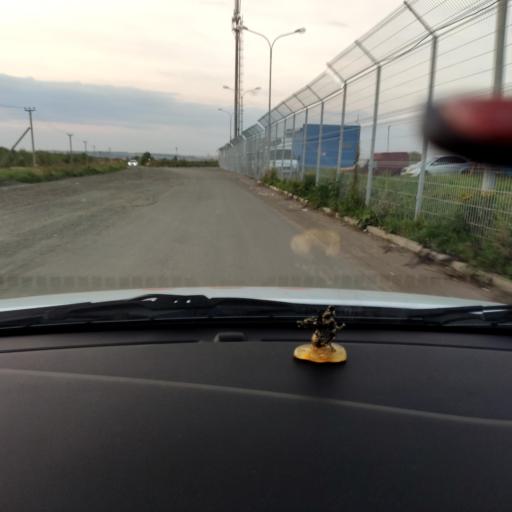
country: RU
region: Tatarstan
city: Vysokaya Gora
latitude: 55.8055
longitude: 49.3143
